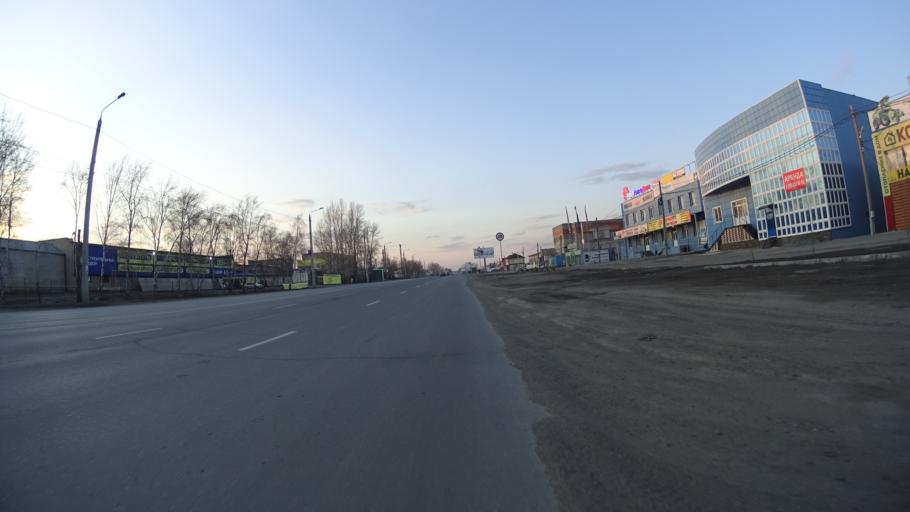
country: RU
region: Chelyabinsk
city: Novosineglazovskiy
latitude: 55.0913
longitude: 61.3883
